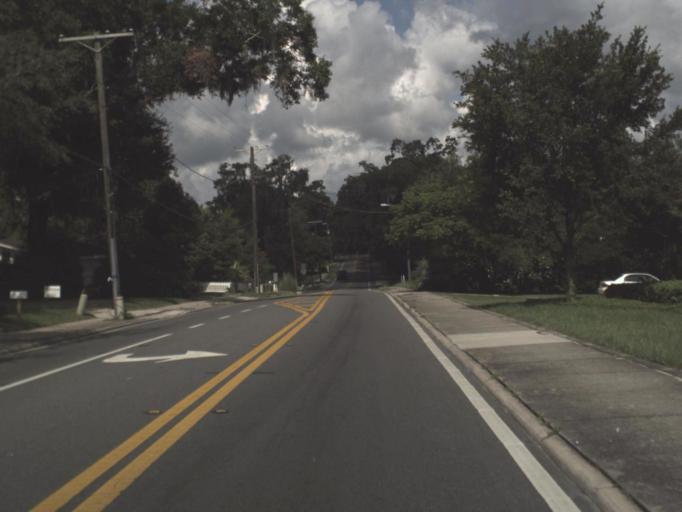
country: US
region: Florida
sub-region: Pasco County
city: Dade City
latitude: 28.3646
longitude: -82.2001
